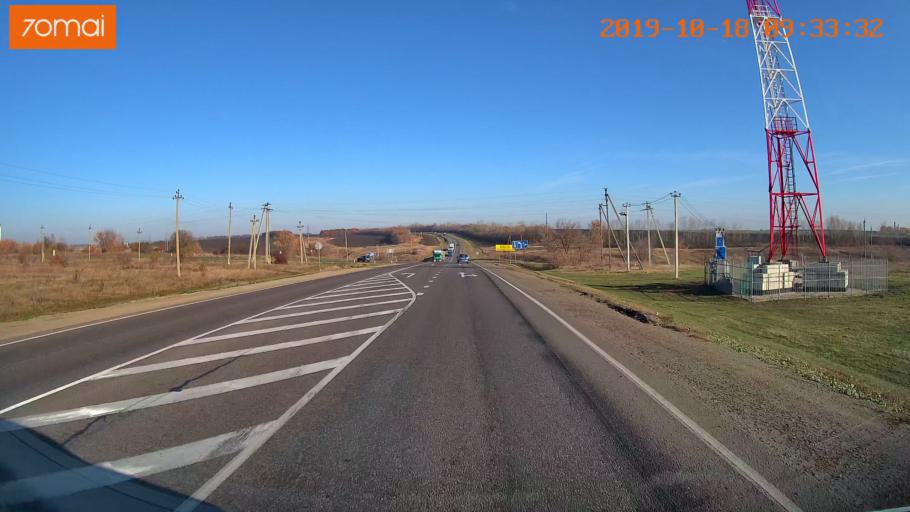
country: RU
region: Tula
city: Yefremov
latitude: 53.1680
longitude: 38.1513
